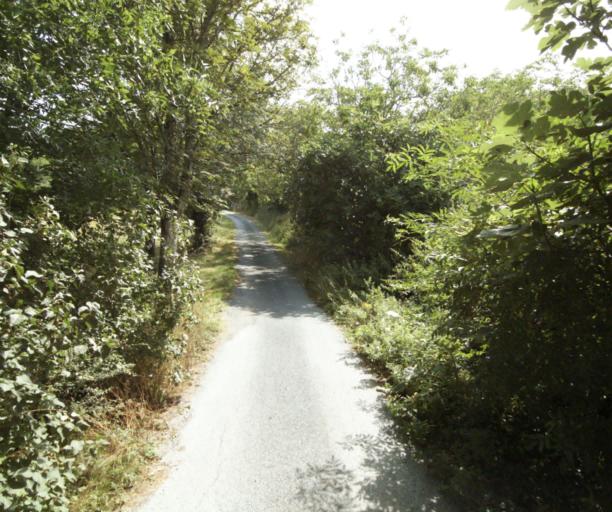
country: FR
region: Midi-Pyrenees
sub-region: Departement du Tarn
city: Soreze
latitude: 43.4615
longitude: 2.0922
